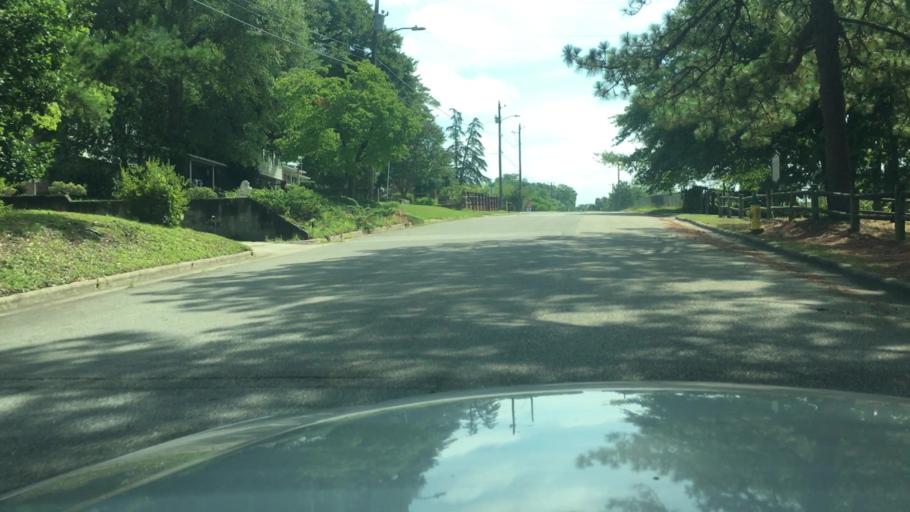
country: US
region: North Carolina
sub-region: Cumberland County
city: Fayetteville
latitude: 35.0297
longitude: -78.9007
